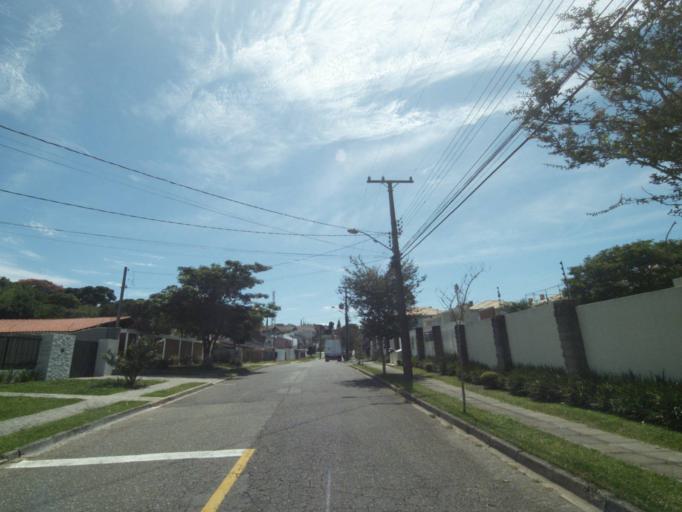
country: BR
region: Parana
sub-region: Curitiba
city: Curitiba
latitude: -25.4627
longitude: -49.2415
